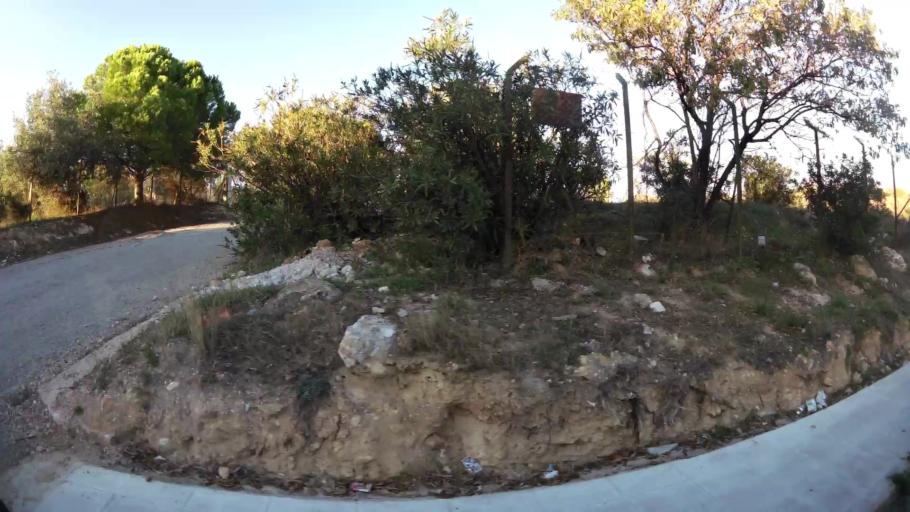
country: GR
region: Attica
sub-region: Nomarchia Anatolikis Attikis
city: Spata
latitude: 37.9668
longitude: 23.9184
